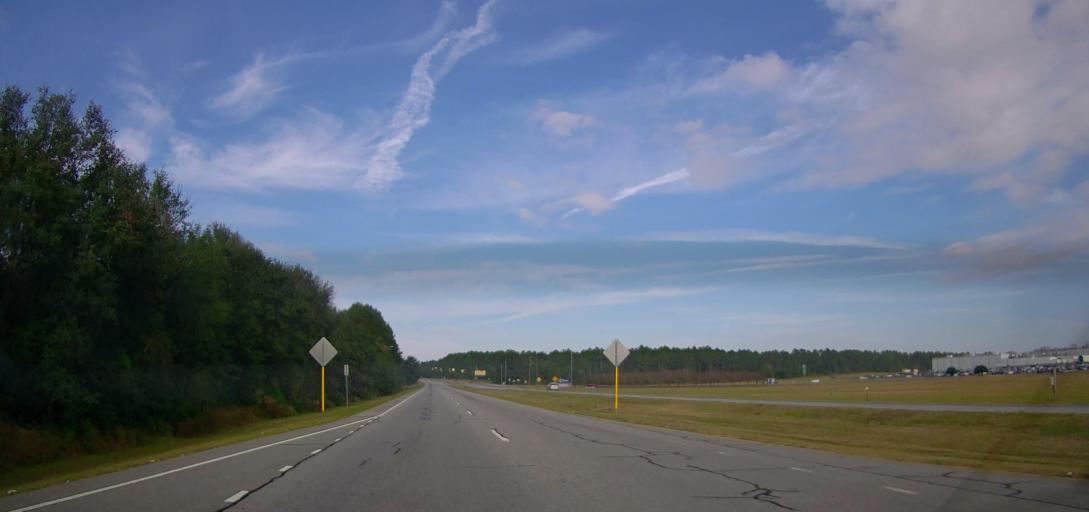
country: US
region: Georgia
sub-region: Mitchell County
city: Camilla
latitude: 31.2787
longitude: -84.1892
